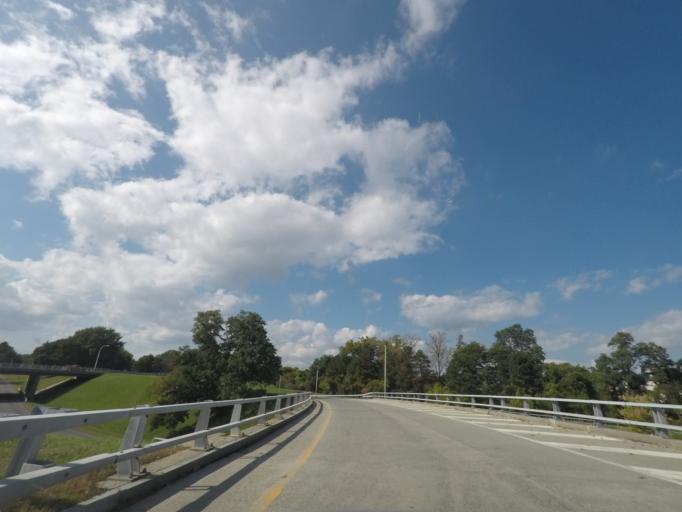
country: US
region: New York
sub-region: Albany County
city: Roessleville
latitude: 42.6850
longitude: -73.8101
